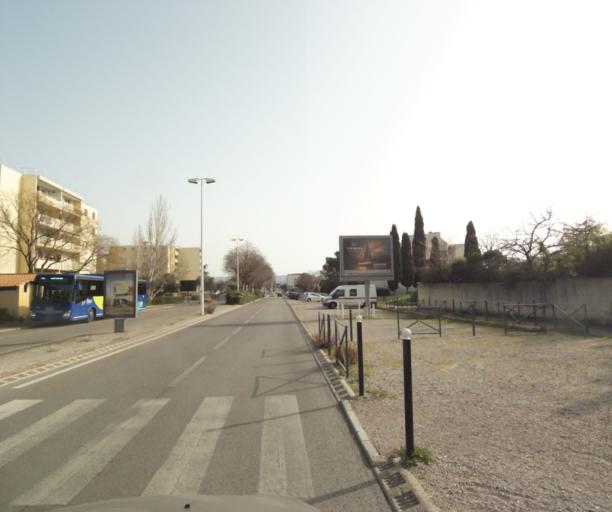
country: FR
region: Provence-Alpes-Cote d'Azur
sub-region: Departement des Bouches-du-Rhone
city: Vitrolles
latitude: 43.4502
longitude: 5.2454
